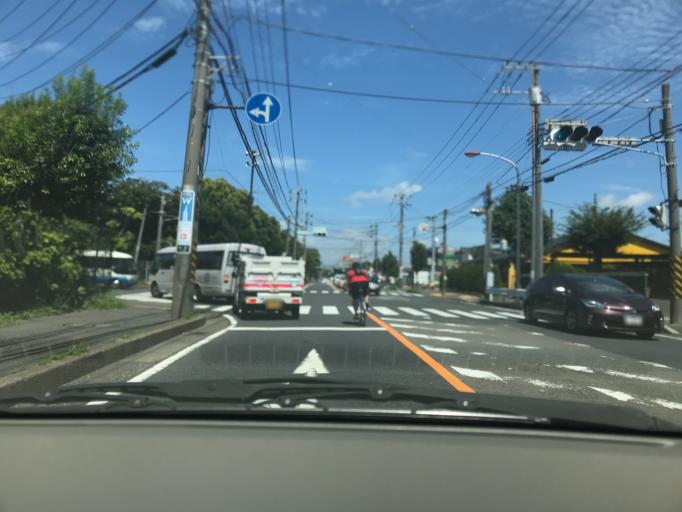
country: JP
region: Kanagawa
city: Fujisawa
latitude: 35.3539
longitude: 139.4673
